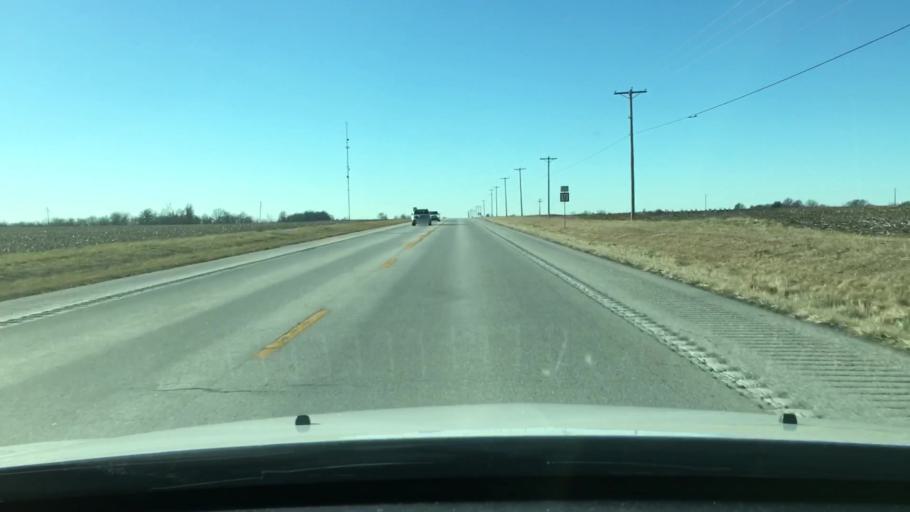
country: US
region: Missouri
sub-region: Pike County
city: Bowling Green
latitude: 39.3446
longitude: -91.2927
